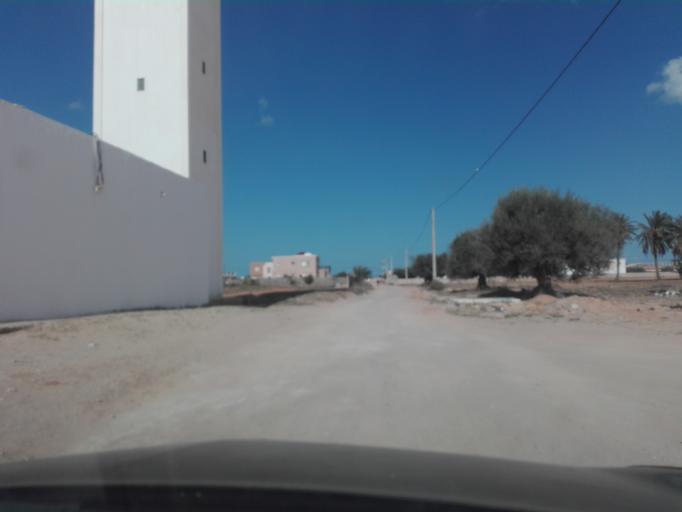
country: TN
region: Madanin
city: Bin Qirdan
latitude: 33.1600
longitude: 11.1949
